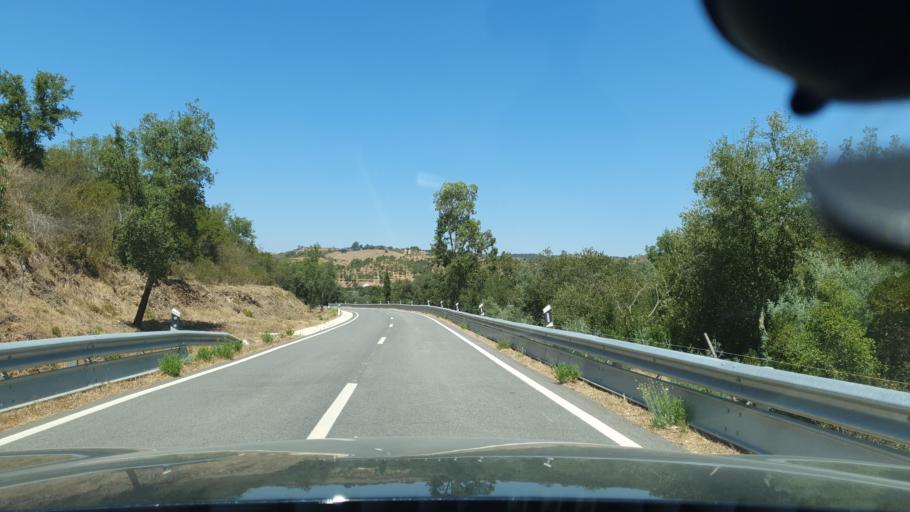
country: PT
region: Beja
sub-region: Odemira
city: Odemira
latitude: 37.5564
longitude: -8.4860
